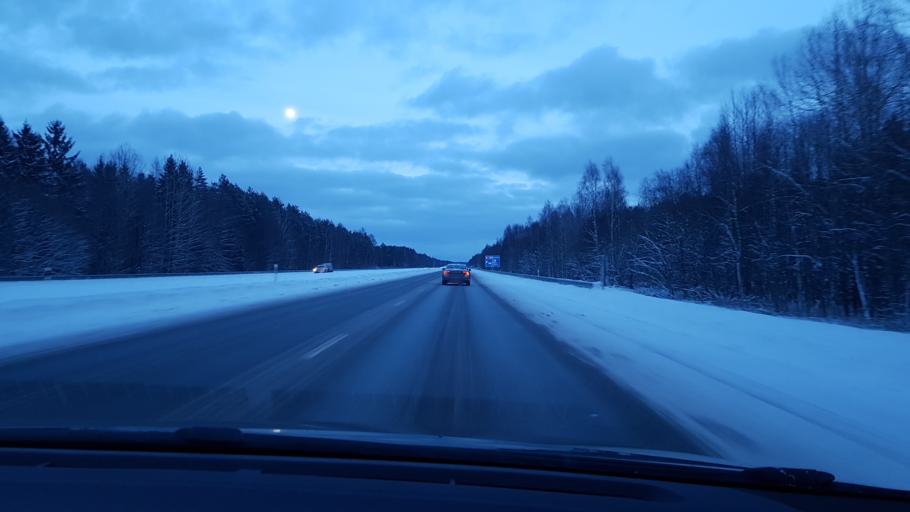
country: EE
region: Harju
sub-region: Kuusalu vald
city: Kuusalu
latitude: 59.4594
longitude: 25.5739
